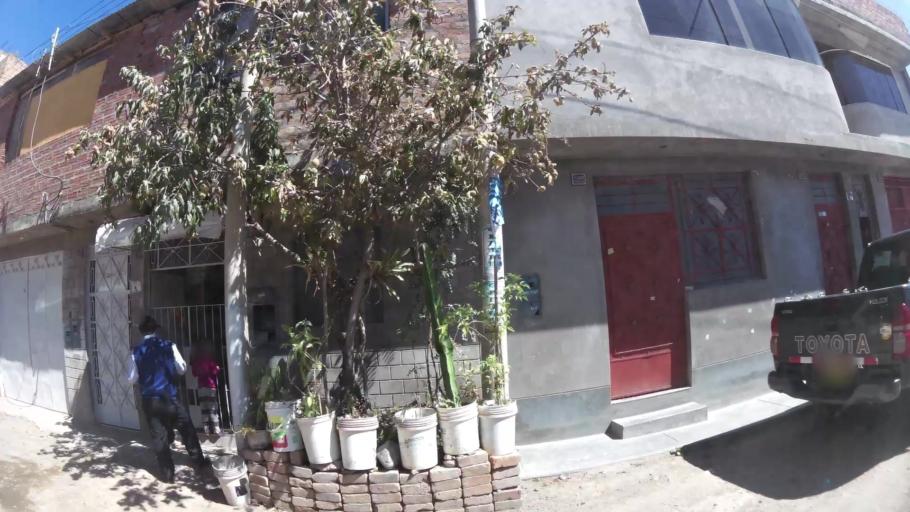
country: PE
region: Ayacucho
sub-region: Provincia de Huamanga
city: Ayacucho
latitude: -13.1538
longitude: -74.2320
